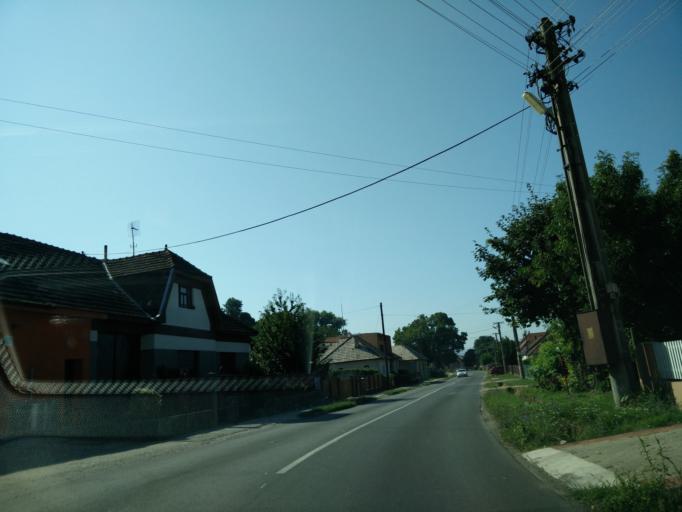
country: SK
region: Nitriansky
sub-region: Okres Nitra
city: Nitra
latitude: 48.4672
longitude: 18.1448
